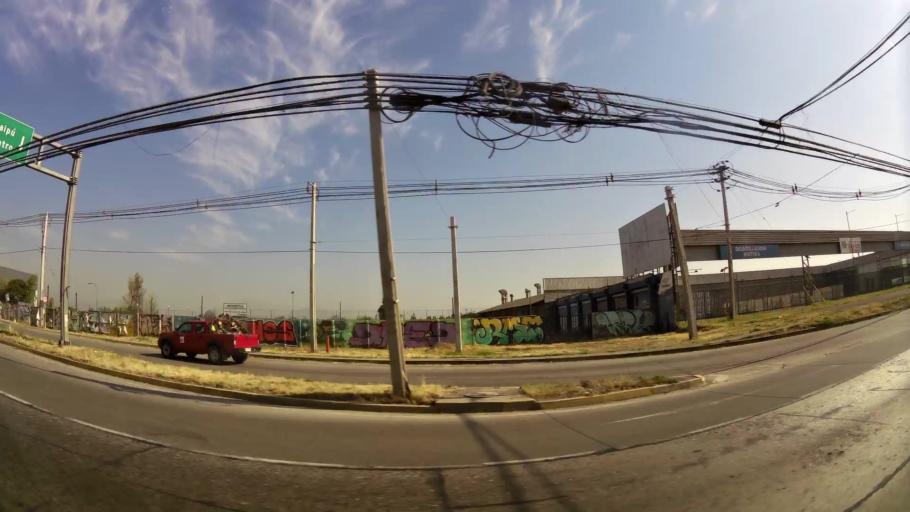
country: CL
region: Santiago Metropolitan
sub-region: Provincia de Santiago
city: Lo Prado
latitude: -33.5248
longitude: -70.7521
